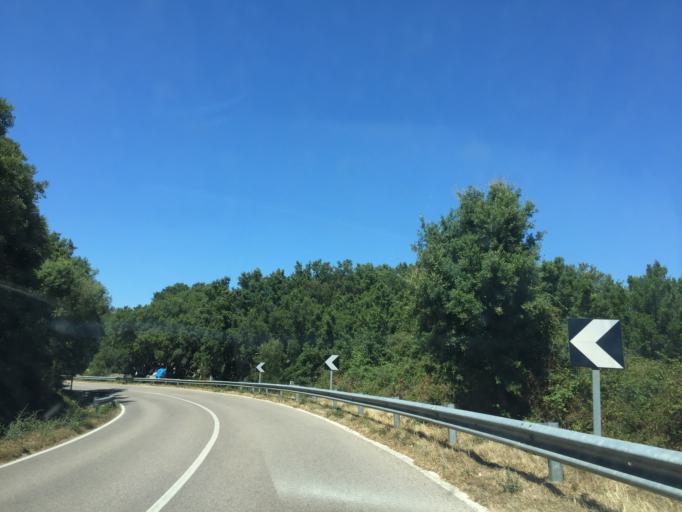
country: IT
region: Sardinia
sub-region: Provincia di Olbia-Tempio
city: Aggius
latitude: 40.9750
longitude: 9.0943
